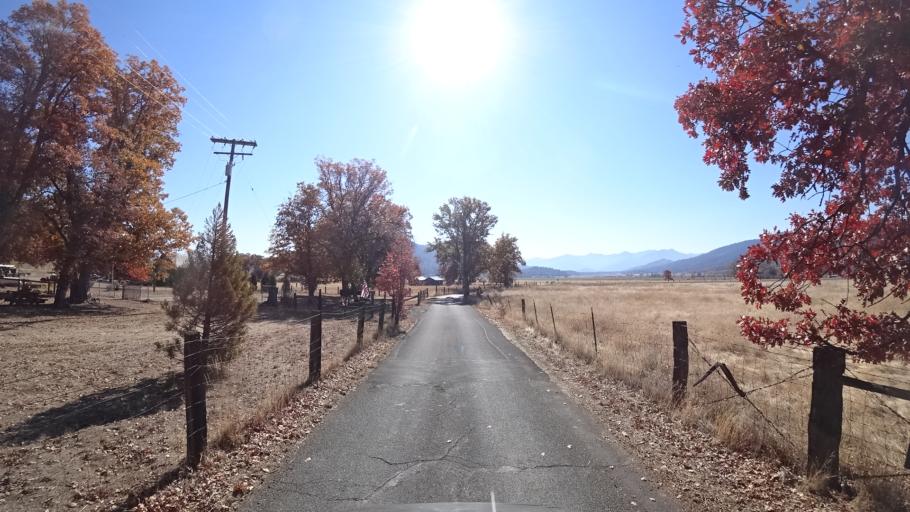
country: US
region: California
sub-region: Siskiyou County
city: Yreka
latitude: 41.6314
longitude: -122.8894
